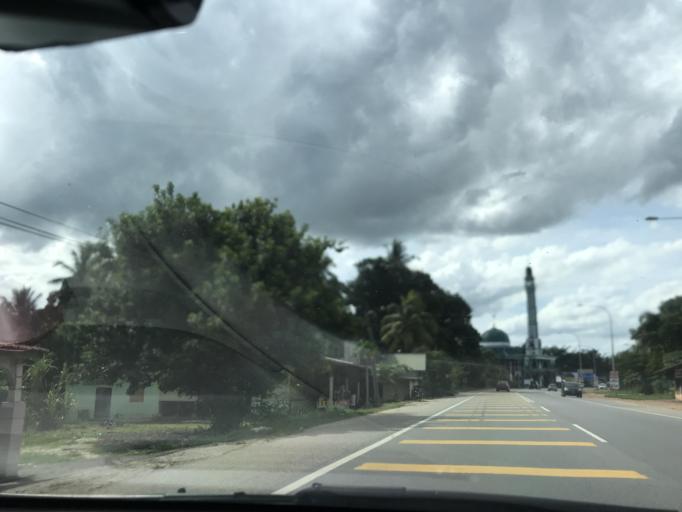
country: MY
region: Kelantan
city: Kampong Pangkal Kalong
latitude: 5.9424
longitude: 102.1913
